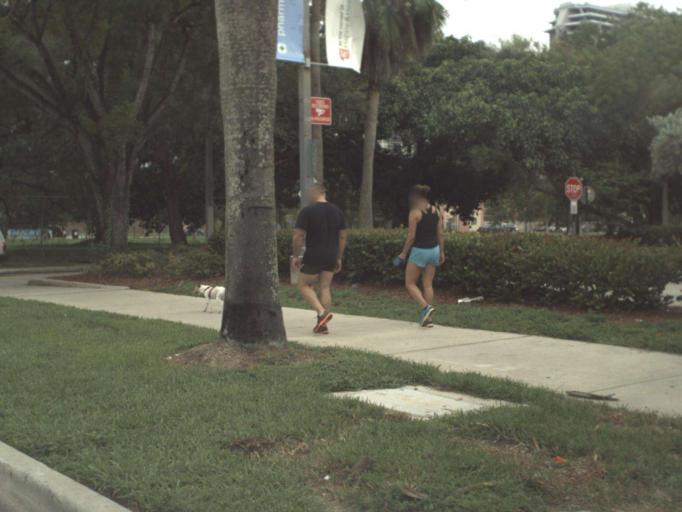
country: US
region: Florida
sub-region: Miami-Dade County
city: Miami
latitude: 25.8069
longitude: -80.1894
